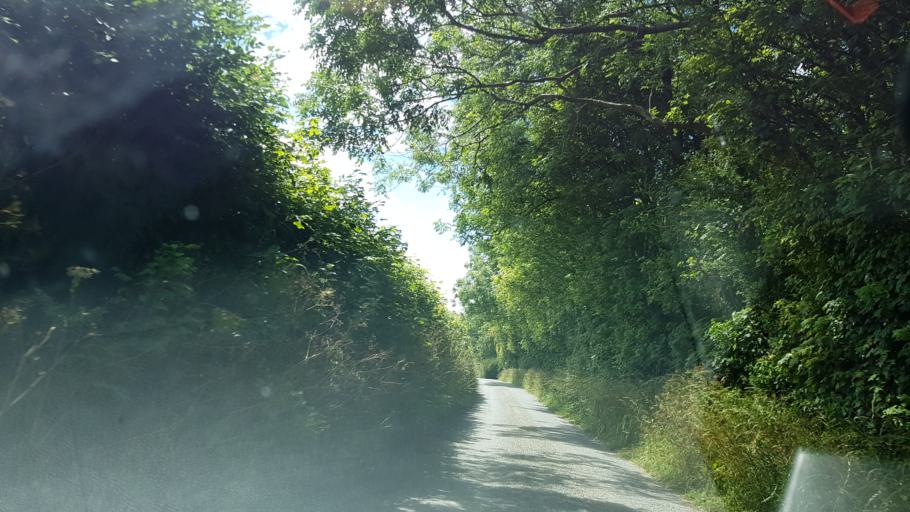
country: GB
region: Wales
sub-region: Pembrokeshire
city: Wiston
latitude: 51.8275
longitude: -4.9041
